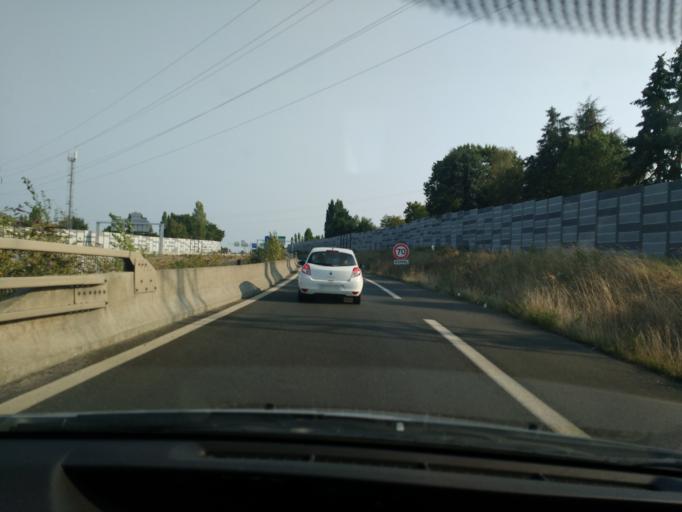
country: FR
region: Pays de la Loire
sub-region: Departement de Maine-et-Loire
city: Ecouflant
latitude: 47.5009
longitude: -0.5024
